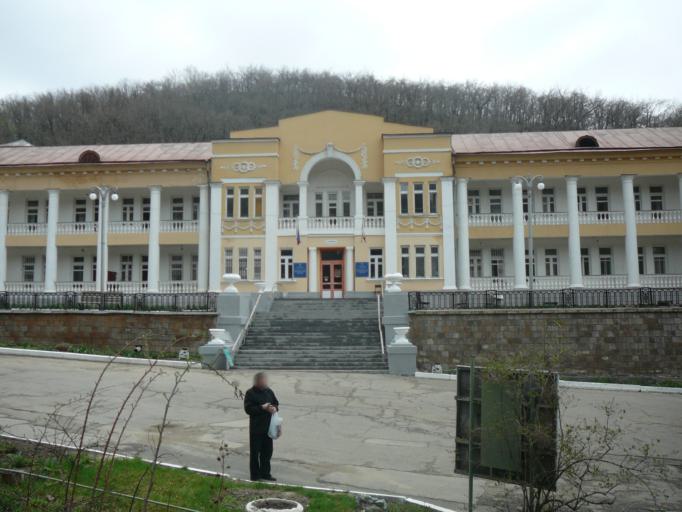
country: RU
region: Saratov
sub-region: Saratovskiy Rayon
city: Saratov
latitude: 51.5490
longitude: 45.9561
